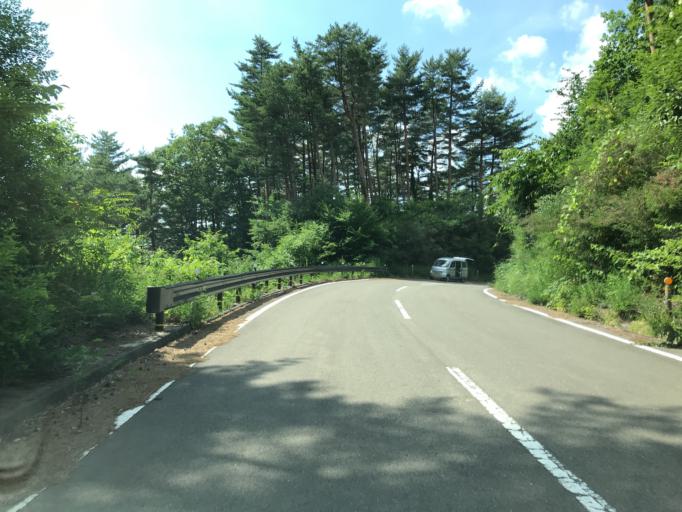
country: JP
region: Fukushima
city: Yanagawamachi-saiwaicho
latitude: 37.7631
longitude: 140.6777
